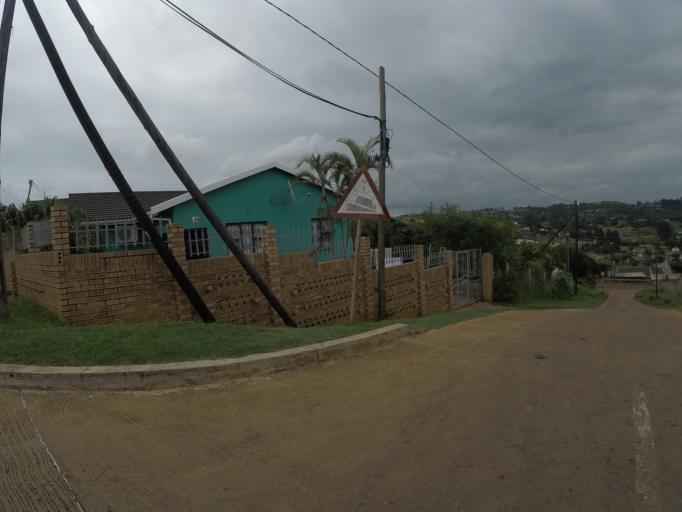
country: ZA
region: KwaZulu-Natal
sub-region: uThungulu District Municipality
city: Empangeni
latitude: -28.7685
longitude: 31.8599
